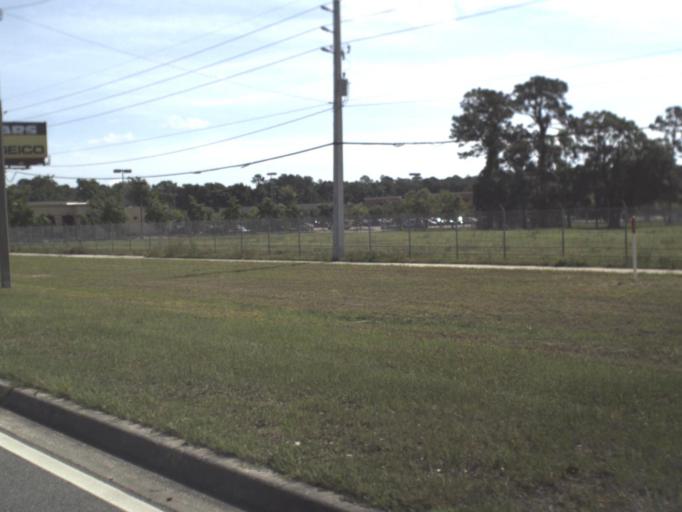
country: US
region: Florida
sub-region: Clay County
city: Orange Park
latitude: 30.2336
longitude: -81.6981
